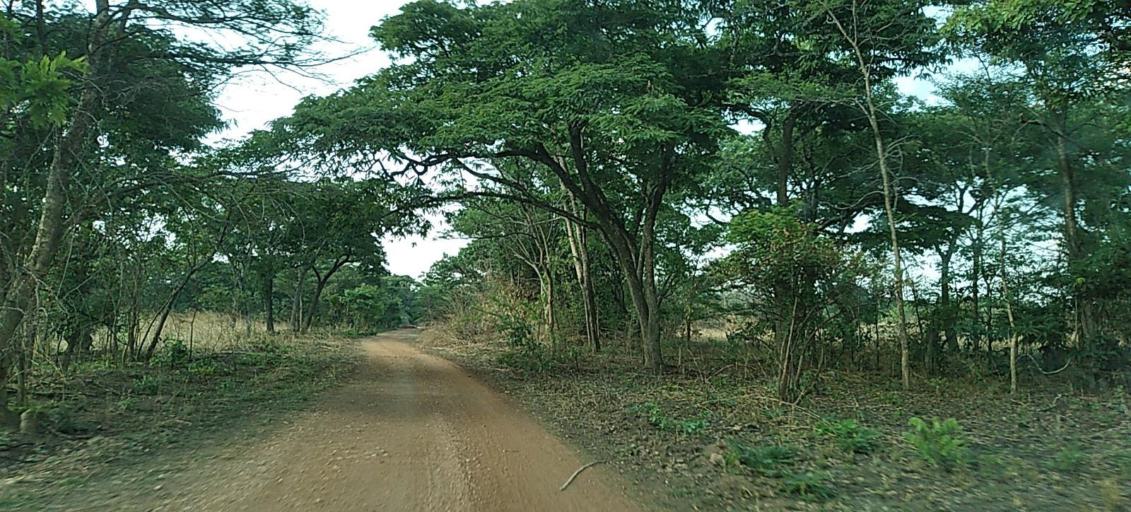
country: ZM
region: Copperbelt
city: Mpongwe
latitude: -13.4662
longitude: 28.0693
